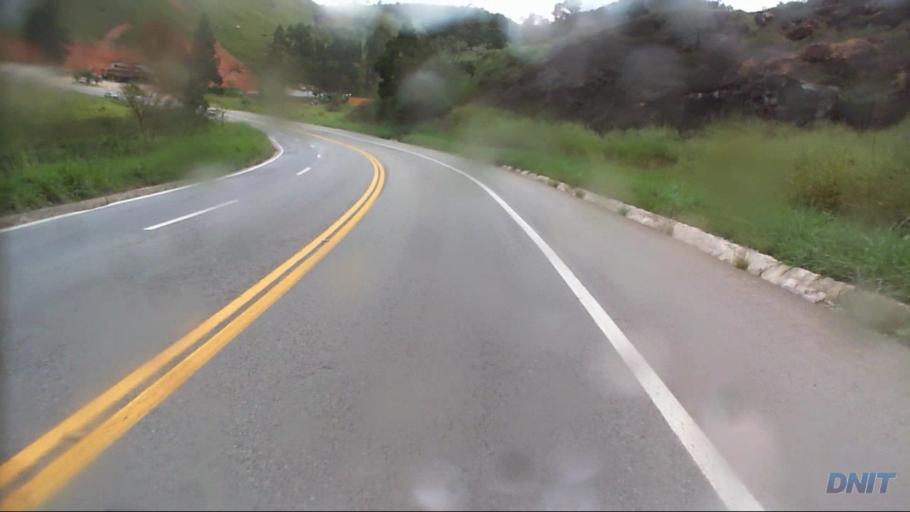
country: BR
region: Minas Gerais
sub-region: Nova Era
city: Nova Era
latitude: -19.6944
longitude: -42.9948
